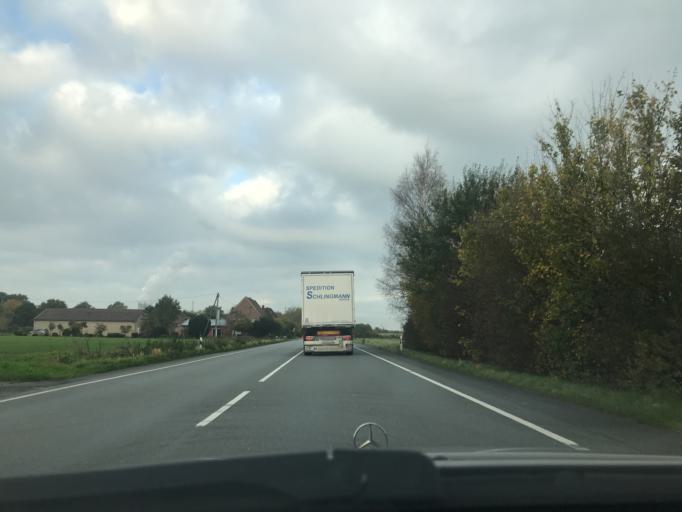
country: DE
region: North Rhine-Westphalia
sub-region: Regierungsbezirk Arnsberg
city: Welver
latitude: 51.6704
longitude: 8.0219
